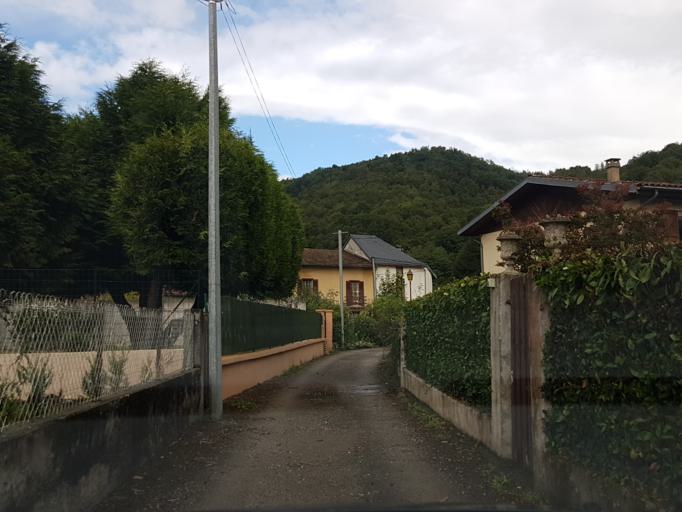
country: FR
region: Midi-Pyrenees
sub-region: Departement de l'Ariege
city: Saint-Girons
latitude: 42.8931
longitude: 1.2126
